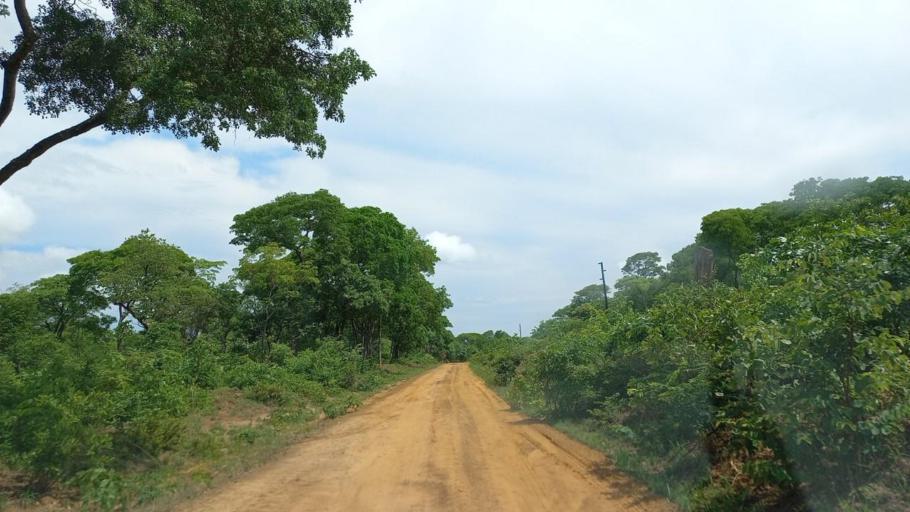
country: ZM
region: North-Western
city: Kabompo
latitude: -13.5375
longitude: 24.0978
